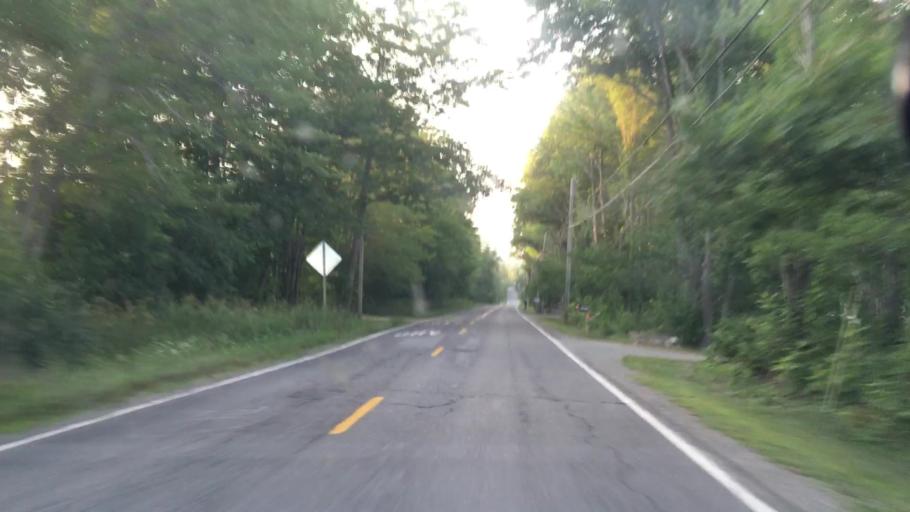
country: US
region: Maine
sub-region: Waldo County
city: Frankfort
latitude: 44.7000
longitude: -68.9453
